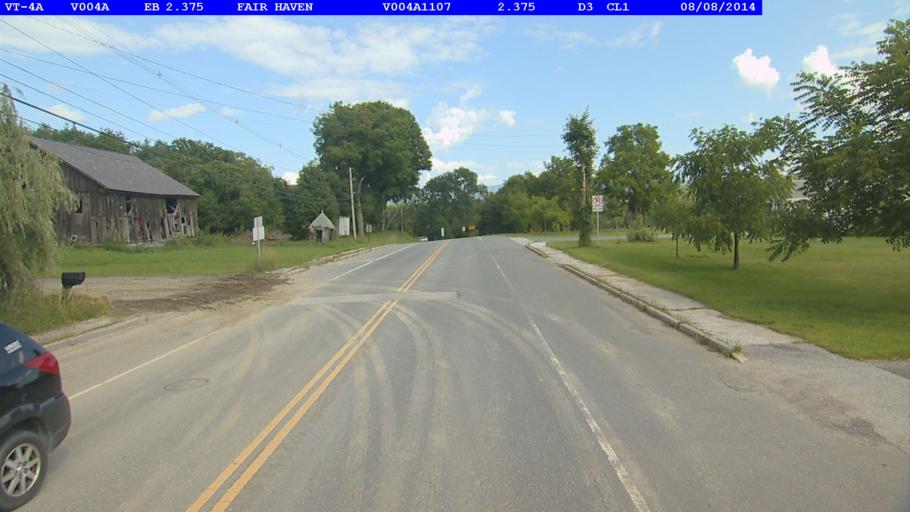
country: US
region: Vermont
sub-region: Rutland County
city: Fair Haven
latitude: 43.5993
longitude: -73.2593
